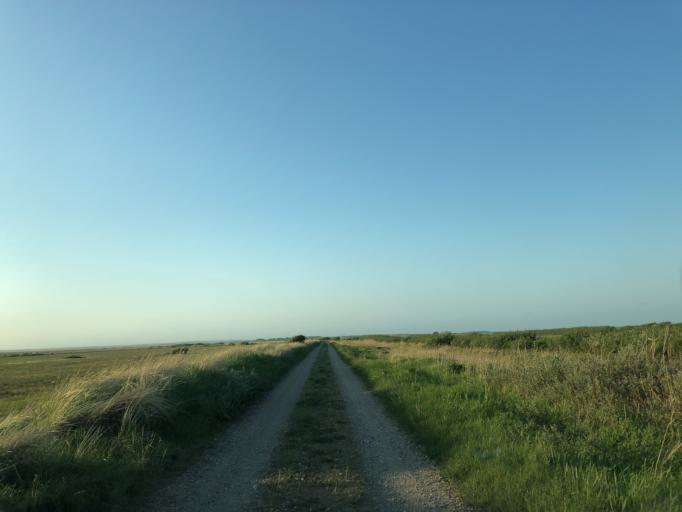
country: DK
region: Central Jutland
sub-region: Ringkobing-Skjern Kommune
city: Ringkobing
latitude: 56.2092
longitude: 8.1622
